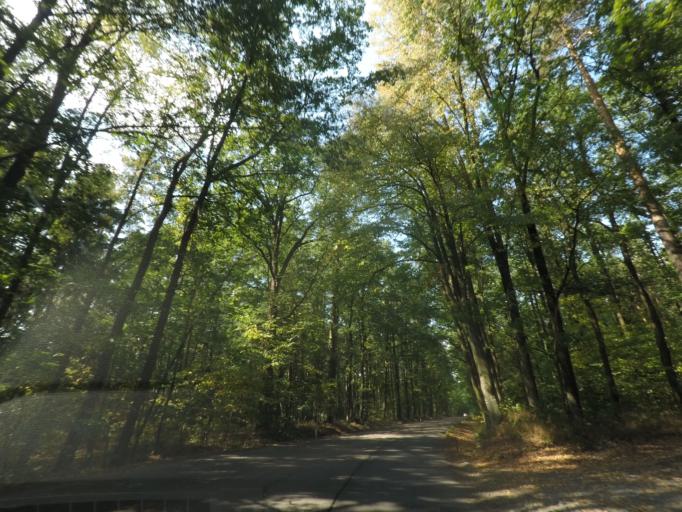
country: CZ
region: Pardubicky
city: Horni Jeleni
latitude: 50.0188
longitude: 16.0813
